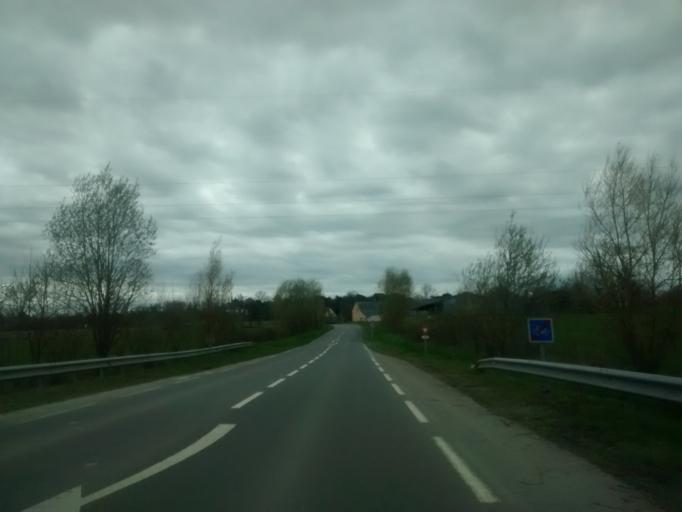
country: FR
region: Brittany
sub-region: Departement d'Ille-et-Vilaine
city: Erce-pres-Liffre
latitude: 48.2400
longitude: -1.5099
